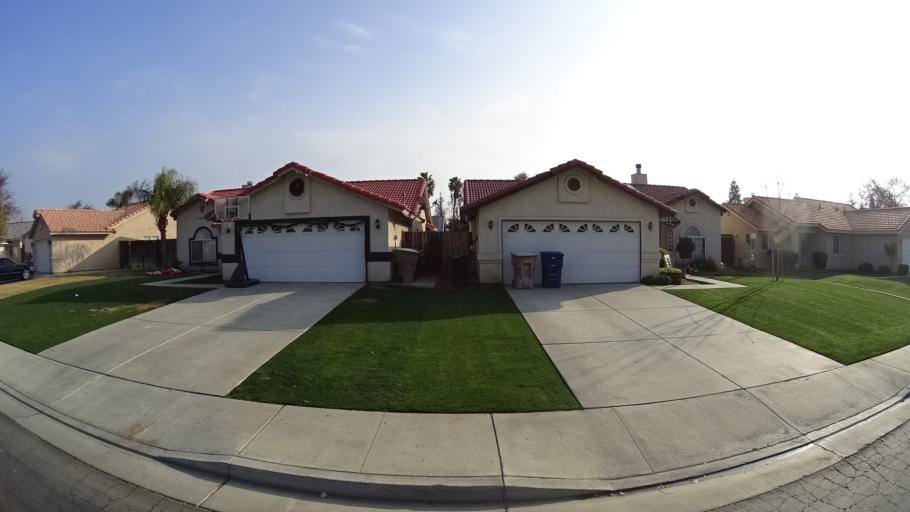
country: US
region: California
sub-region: Kern County
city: Greenfield
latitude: 35.3062
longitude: -119.0696
